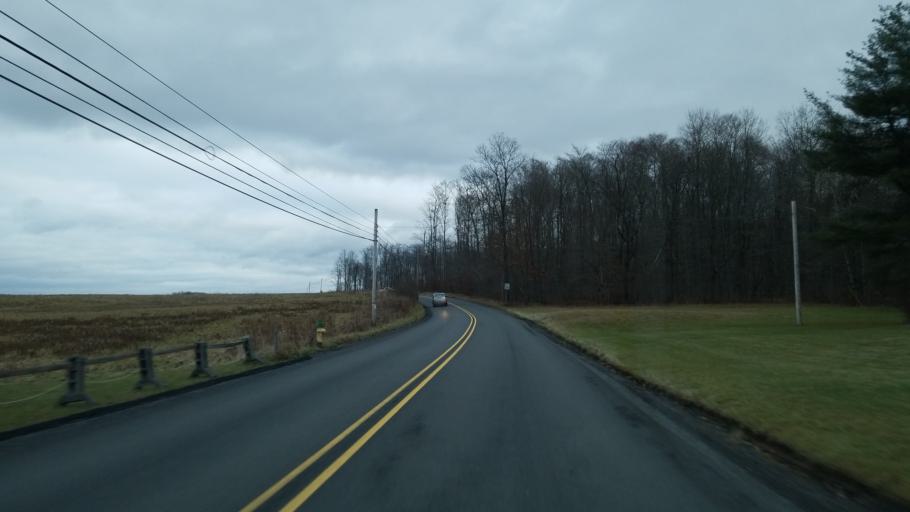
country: US
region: Pennsylvania
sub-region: Jefferson County
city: Falls Creek
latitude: 41.1165
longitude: -78.8008
